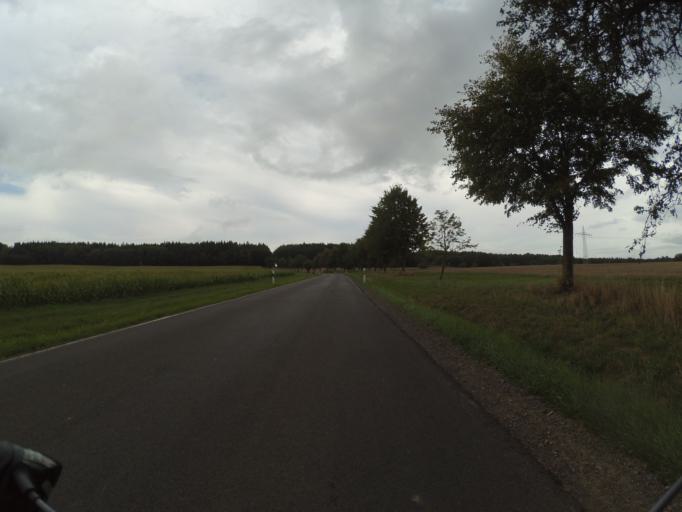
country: DE
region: Rheinland-Pfalz
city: Orenhofen
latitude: 49.9142
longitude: 6.6521
